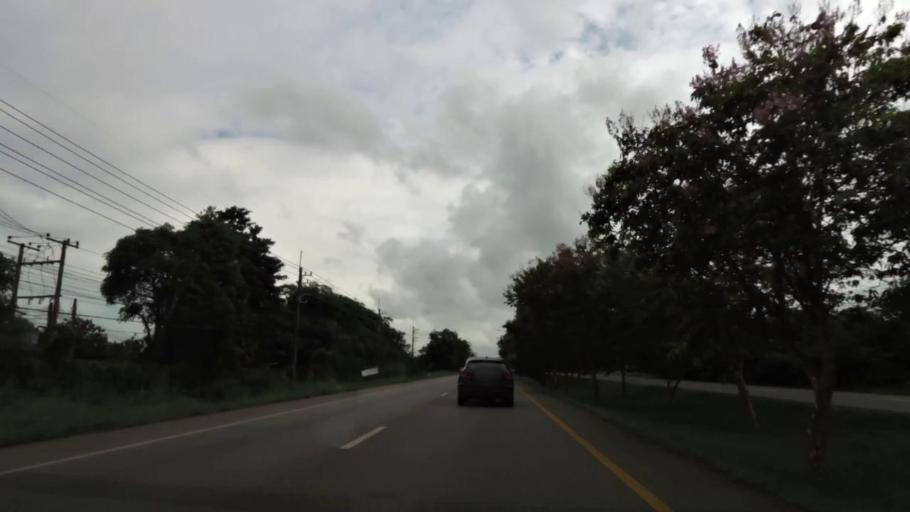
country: TH
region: Chanthaburi
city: Na Yai Am
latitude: 12.7287
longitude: 101.9224
